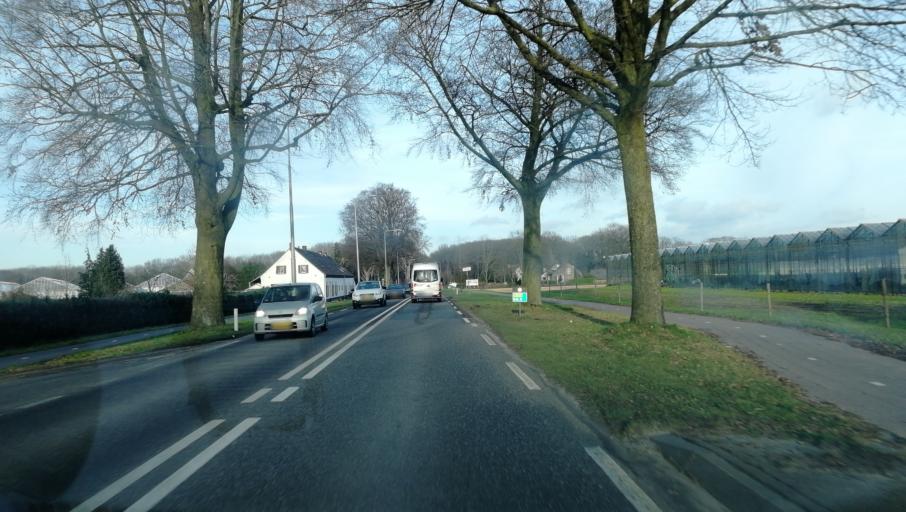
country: NL
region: Limburg
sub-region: Gemeente Venlo
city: Tegelen
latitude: 51.3413
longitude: 6.1026
